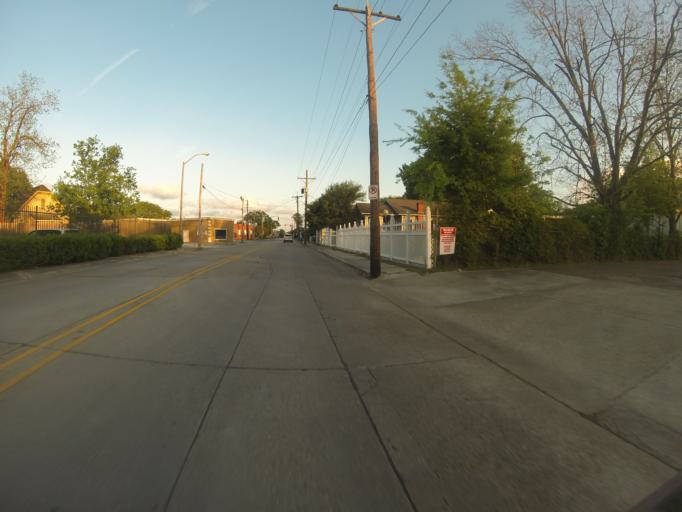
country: US
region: Louisiana
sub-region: Lafayette Parish
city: Lafayette
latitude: 30.2251
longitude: -92.0153
